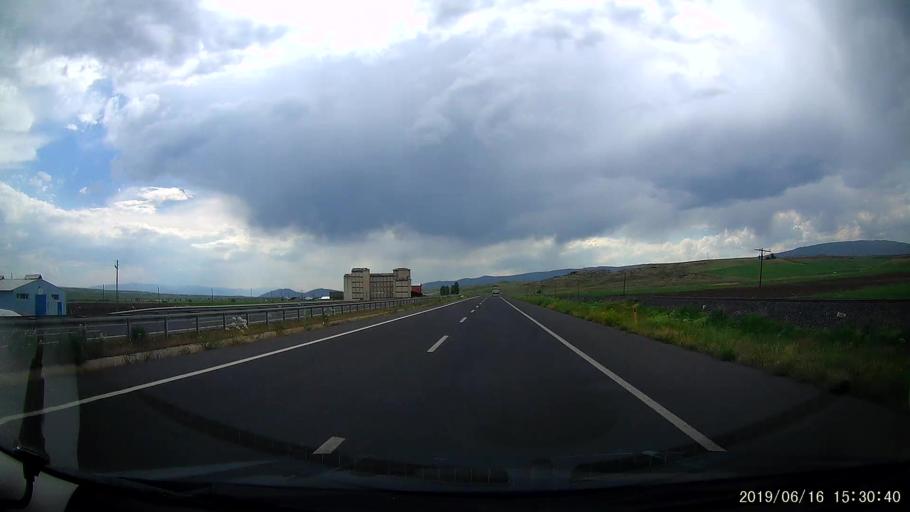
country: TR
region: Erzurum
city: Horasan
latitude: 40.0342
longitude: 42.0986
